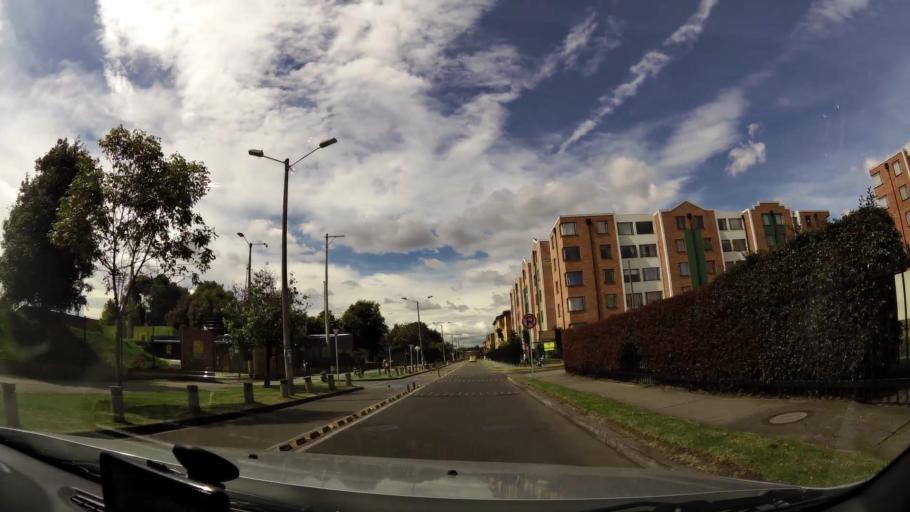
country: CO
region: Bogota D.C.
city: Bogota
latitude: 4.6213
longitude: -74.1339
